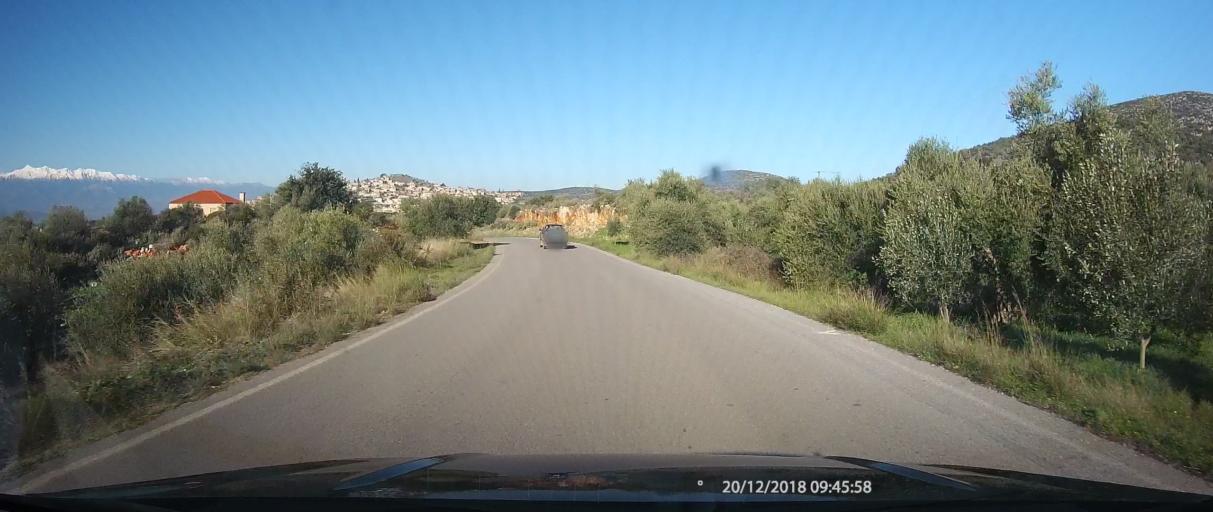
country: GR
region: Peloponnese
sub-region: Nomos Lakonias
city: Yerakion
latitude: 36.9888
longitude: 22.7206
